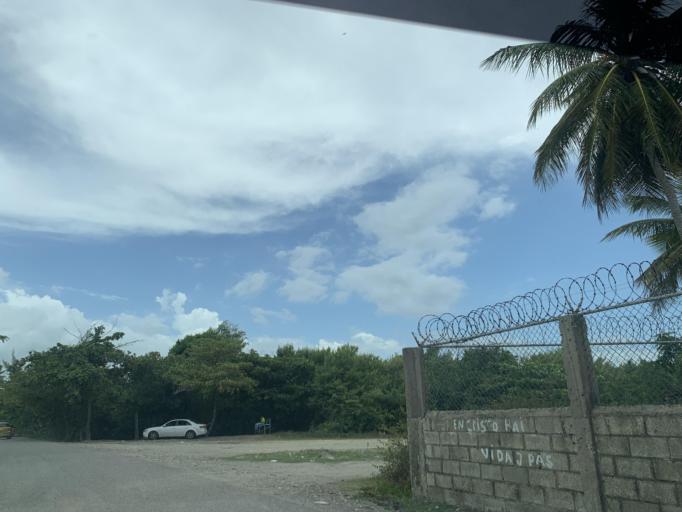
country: DO
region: Puerto Plata
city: Imbert
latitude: 19.8280
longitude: -70.7776
